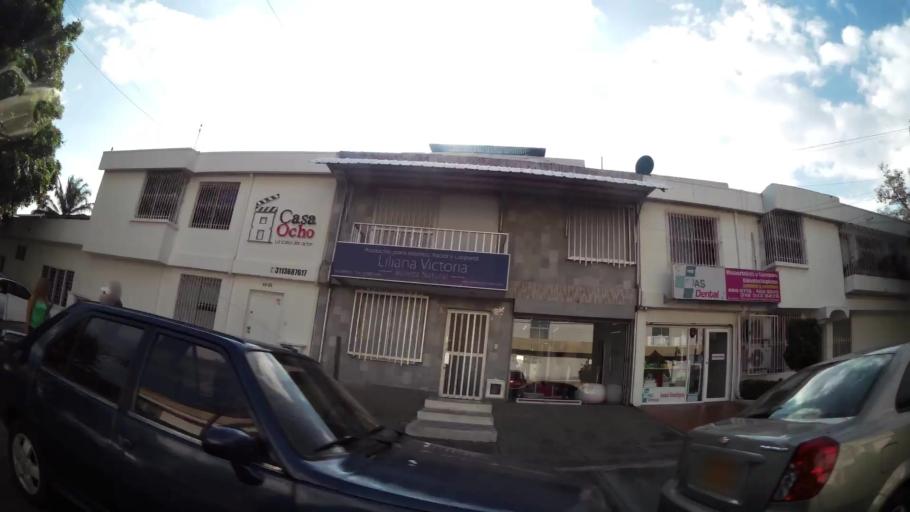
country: CO
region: Valle del Cauca
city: Cali
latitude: 3.4223
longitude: -76.5453
